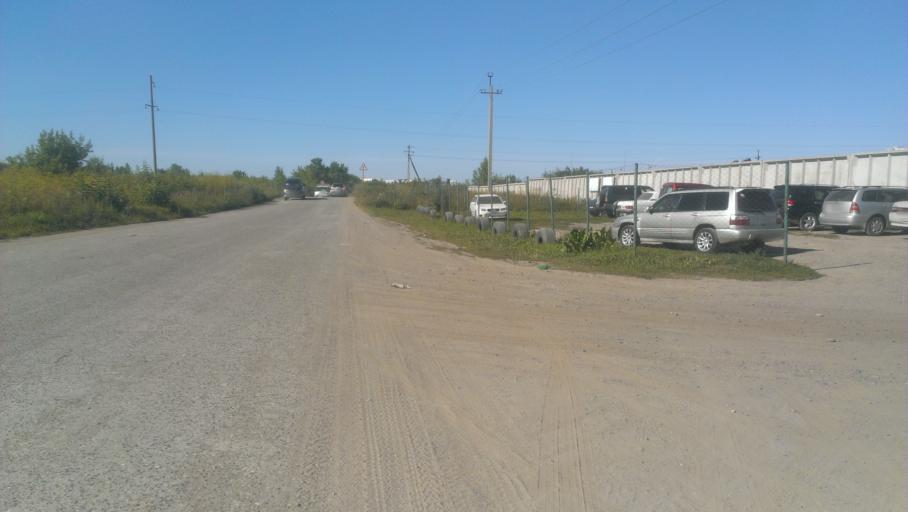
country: RU
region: Altai Krai
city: Novosilikatnyy
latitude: 53.3352
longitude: 83.6352
